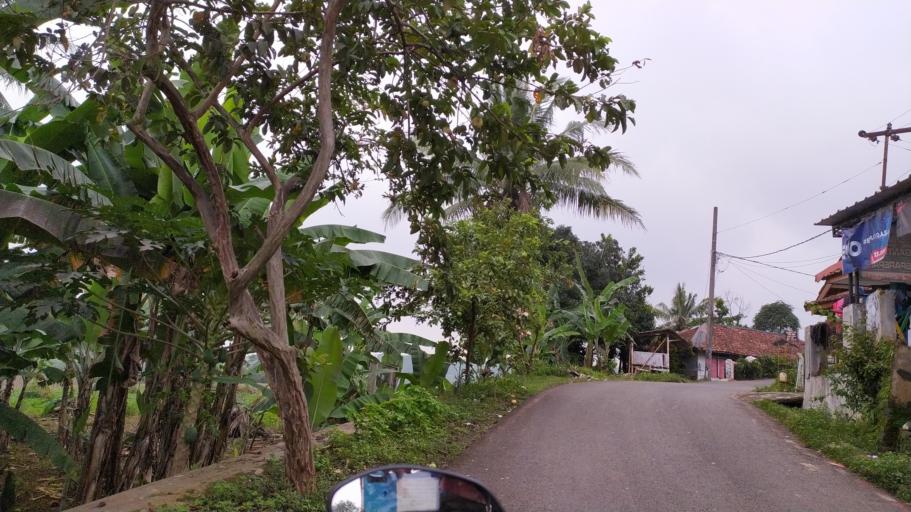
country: ID
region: West Java
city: Ciampea
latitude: -6.6359
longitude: 106.7069
